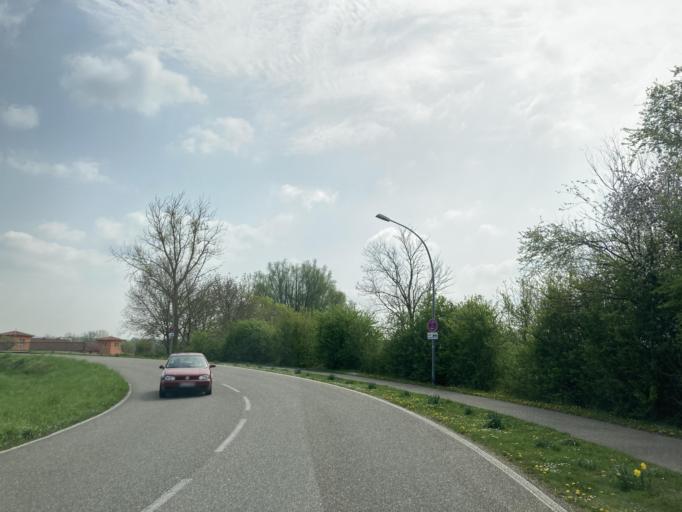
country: DE
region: Baden-Wuerttemberg
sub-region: Karlsruhe Region
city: Kronau
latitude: 49.2208
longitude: 8.6433
